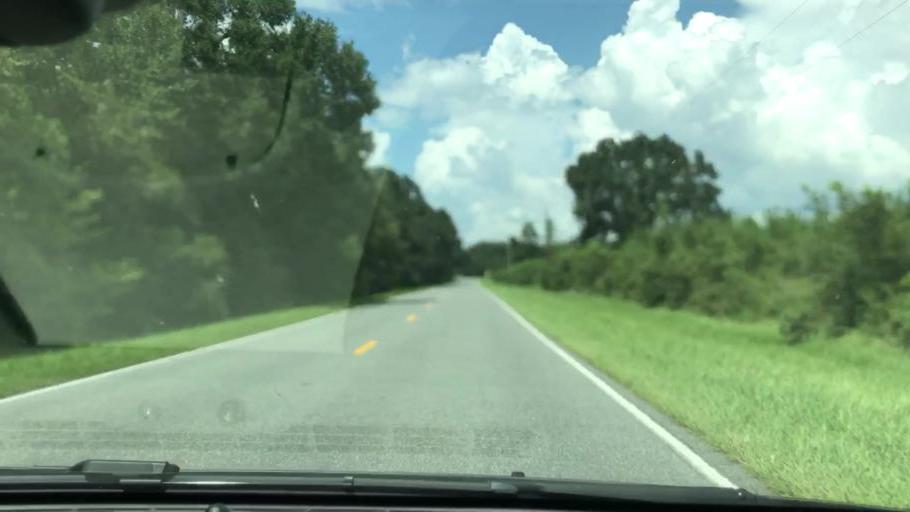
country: US
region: Florida
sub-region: Jackson County
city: Malone
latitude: 30.9367
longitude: -85.1185
